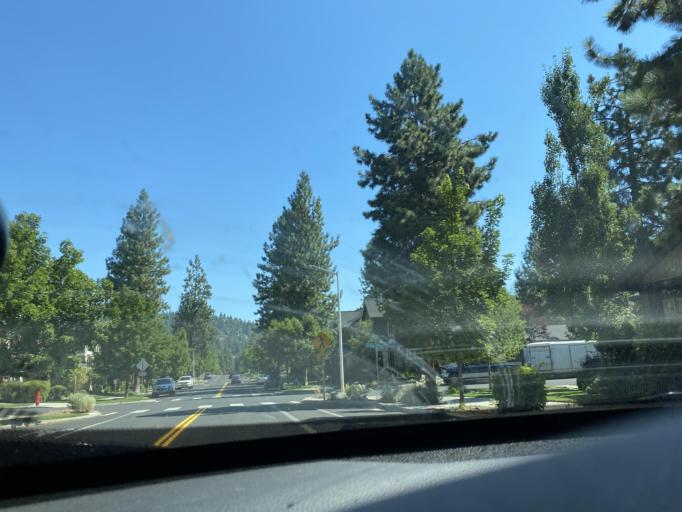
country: US
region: Oregon
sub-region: Deschutes County
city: Bend
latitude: 44.0597
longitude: -121.3499
